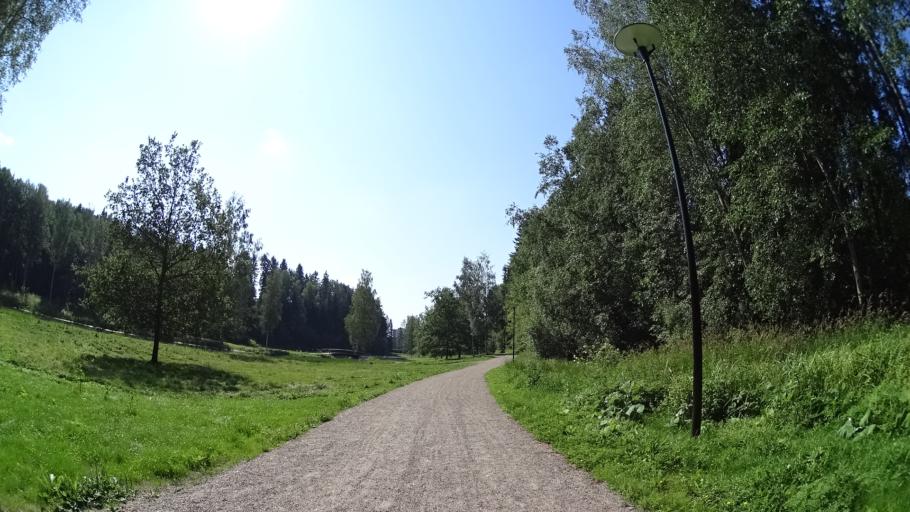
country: FI
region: Uusimaa
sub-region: Helsinki
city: Kerava
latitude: 60.3565
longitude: 25.0727
